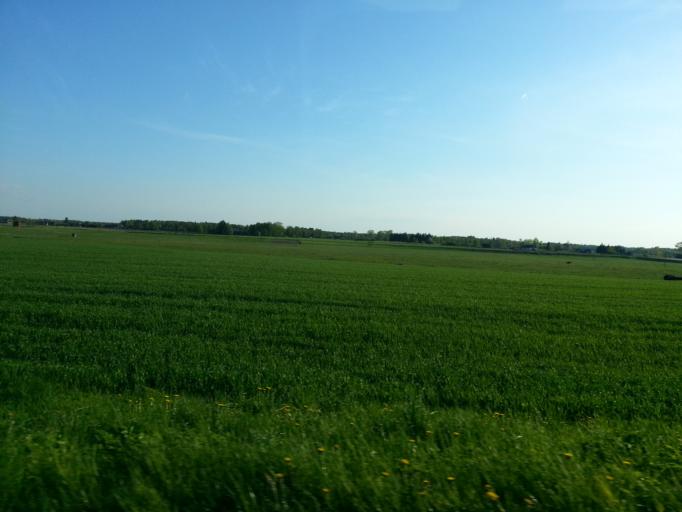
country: LT
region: Vilnius County
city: Ukmerge
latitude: 55.4259
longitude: 24.5951
